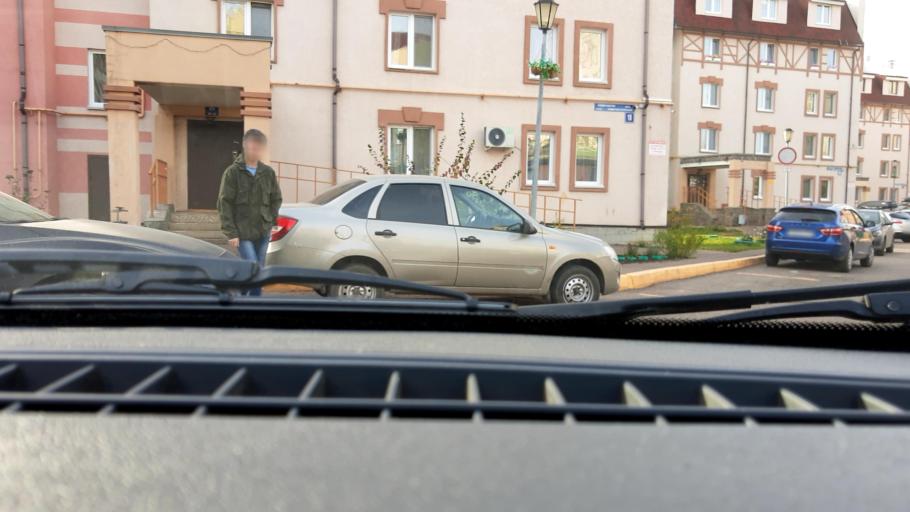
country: RU
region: Bashkortostan
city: Mikhaylovka
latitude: 54.8123
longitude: 55.8969
